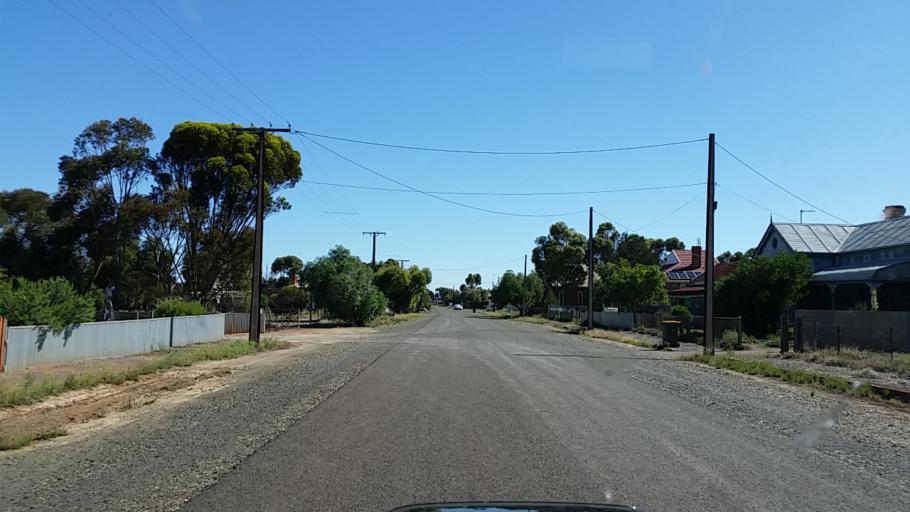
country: AU
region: South Australia
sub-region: Peterborough
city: Peterborough
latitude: -33.1485
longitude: 138.9191
